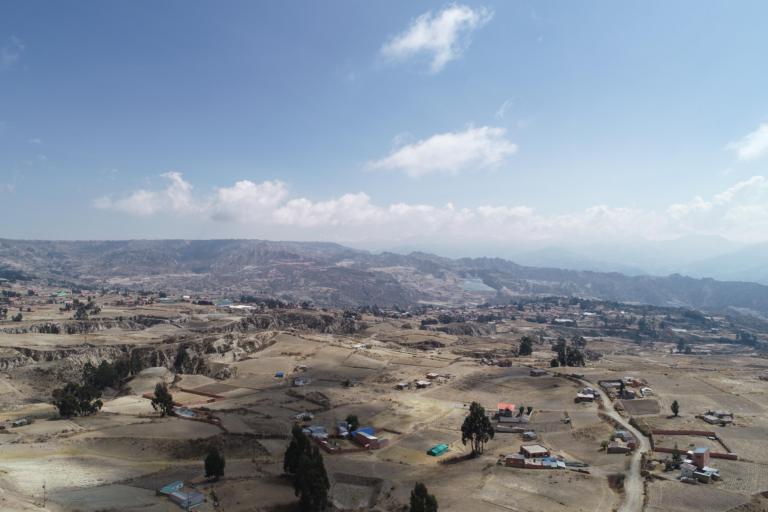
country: BO
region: La Paz
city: La Paz
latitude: -16.6014
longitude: -68.1285
